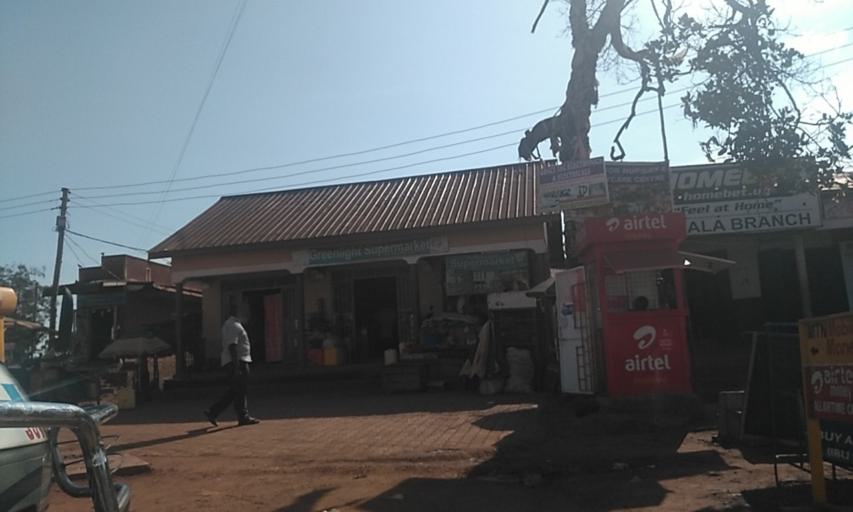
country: UG
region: Central Region
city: Kampala Central Division
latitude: 0.3250
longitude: 32.5394
